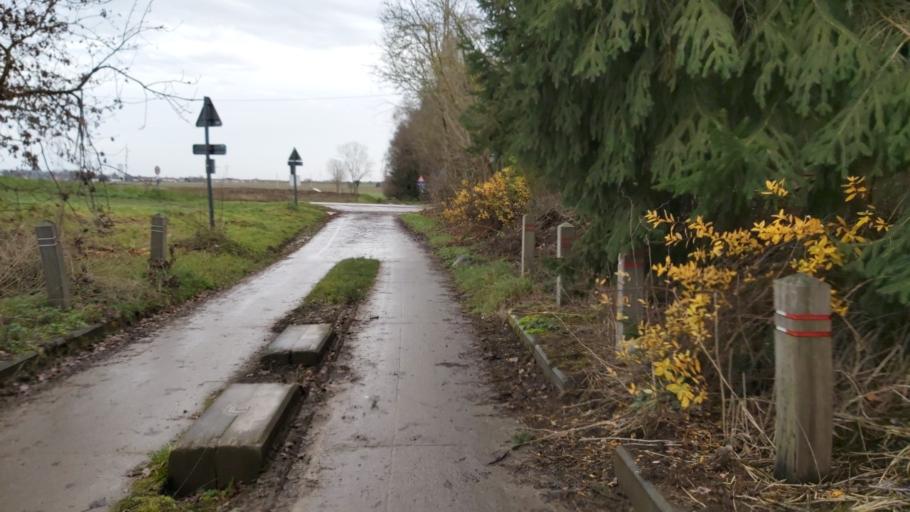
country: BE
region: Flanders
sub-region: Provincie Vlaams-Brabant
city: Tienen
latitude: 50.8268
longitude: 4.8977
